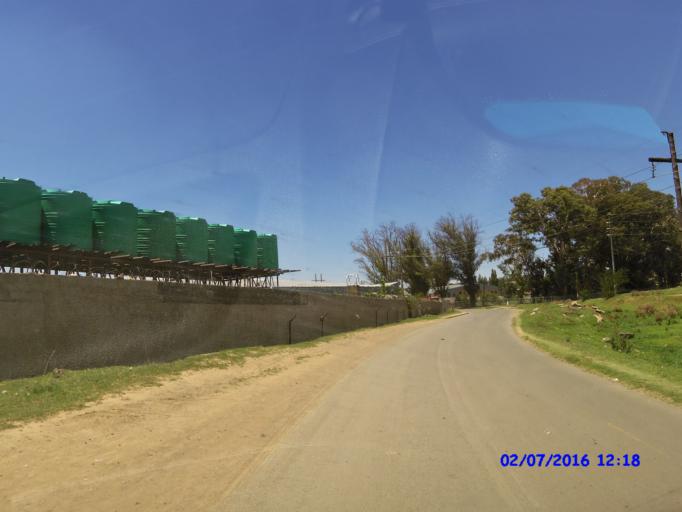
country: LS
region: Maseru
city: Maseru
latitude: -29.2964
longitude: 27.4656
